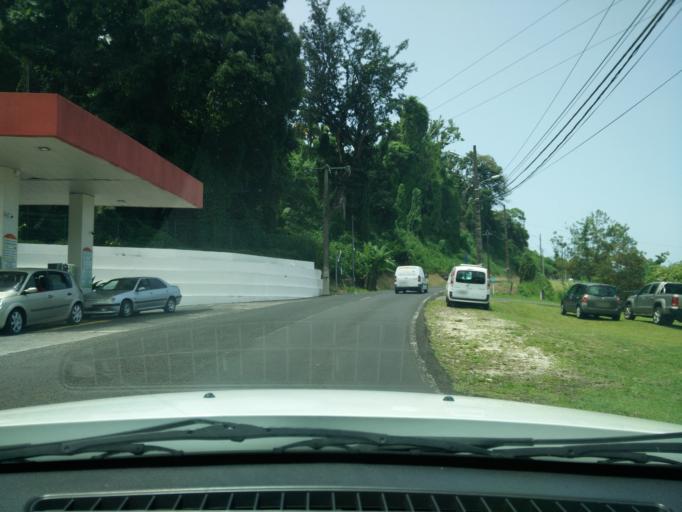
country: GP
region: Guadeloupe
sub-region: Guadeloupe
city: Trois-Rivieres
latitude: 15.9772
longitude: -61.6342
